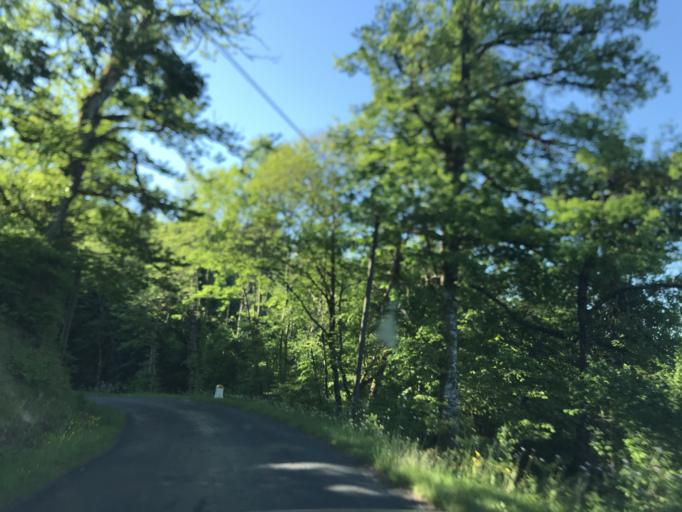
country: FR
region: Auvergne
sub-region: Departement du Puy-de-Dome
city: Job
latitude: 45.6941
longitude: 3.6835
